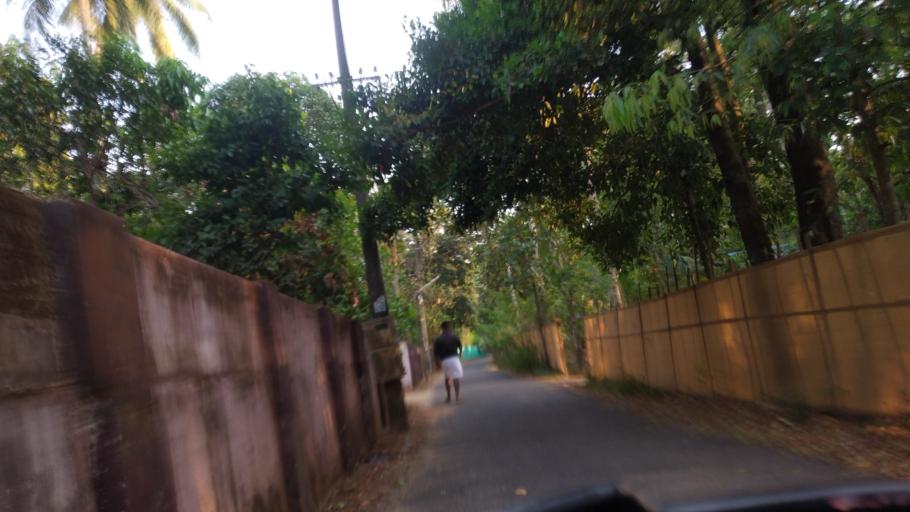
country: IN
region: Kerala
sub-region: Thrissur District
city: Thanniyam
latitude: 10.4135
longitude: 76.0877
